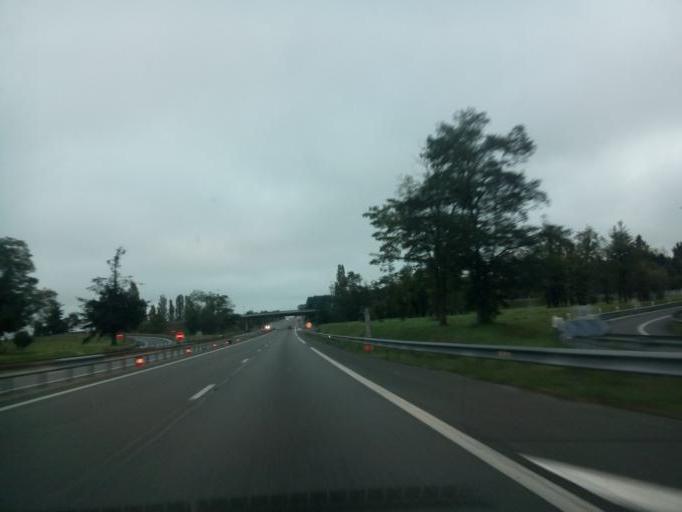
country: FR
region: Rhone-Alpes
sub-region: Departement de l'Isere
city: Saint-Jean-de-Soudain
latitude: 45.5605
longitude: 5.4232
